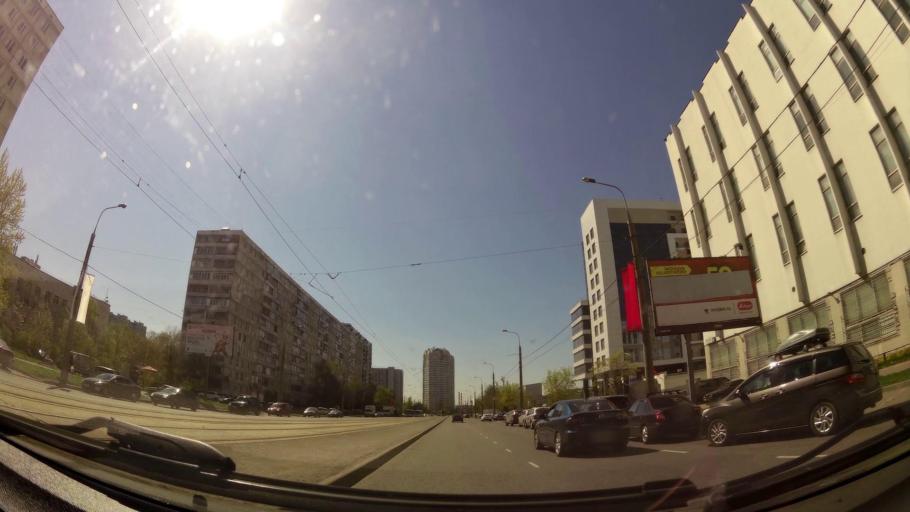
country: RU
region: Moscow
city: Strogino
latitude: 55.8038
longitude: 37.3927
